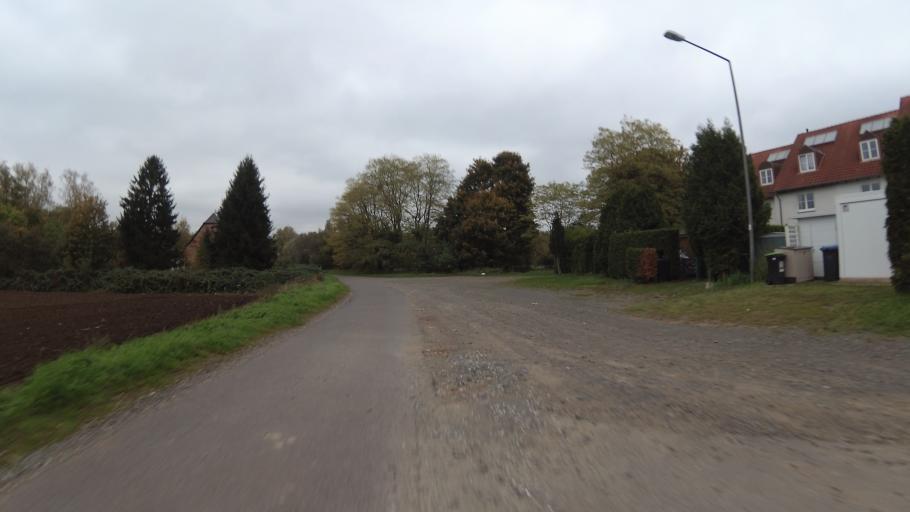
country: DE
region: Saarland
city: Homburg
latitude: 49.3005
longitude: 7.3200
